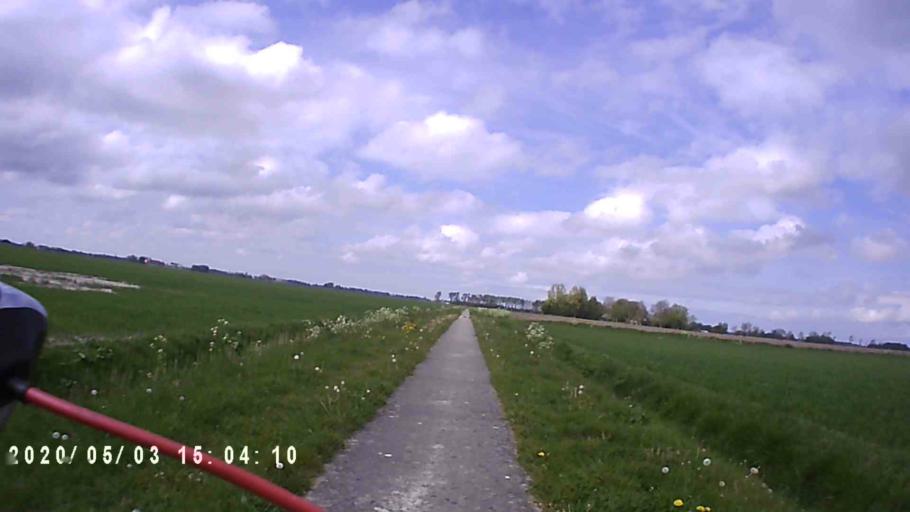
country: NL
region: Groningen
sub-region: Gemeente Zuidhorn
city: Oldehove
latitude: 53.3666
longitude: 6.4432
